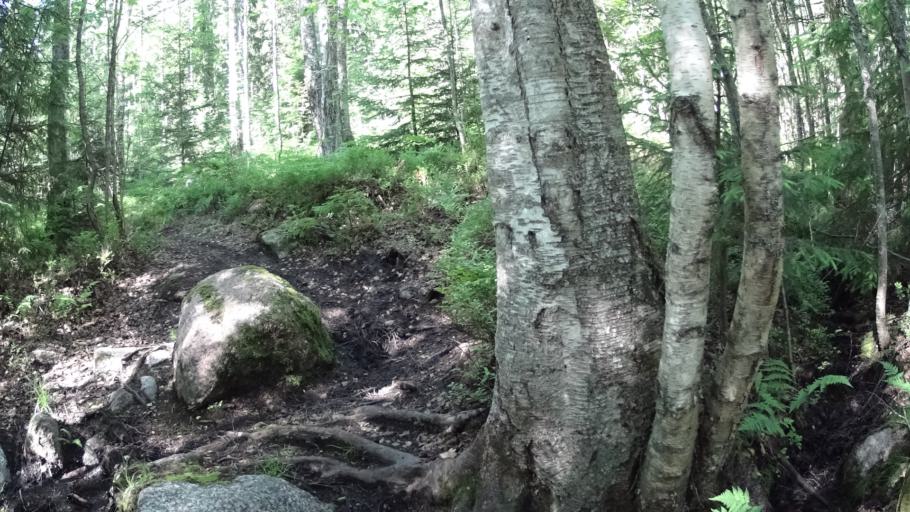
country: FI
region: Uusimaa
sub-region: Helsinki
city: Kilo
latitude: 60.2981
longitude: 24.8367
